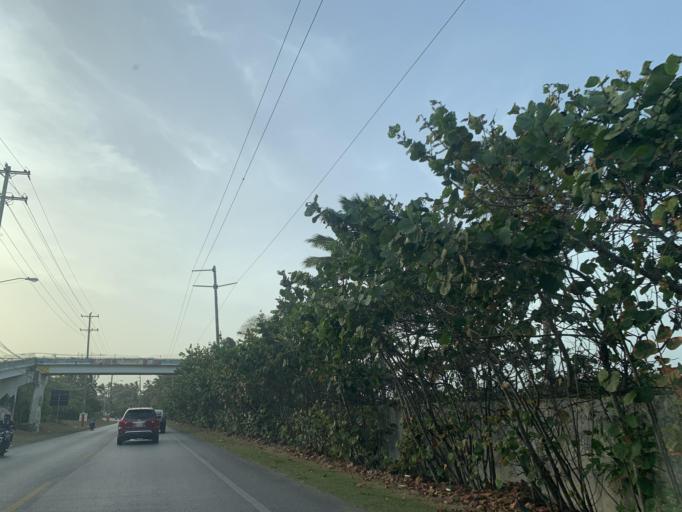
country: DO
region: Puerto Plata
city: Cabarete
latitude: 19.7594
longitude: -70.4199
